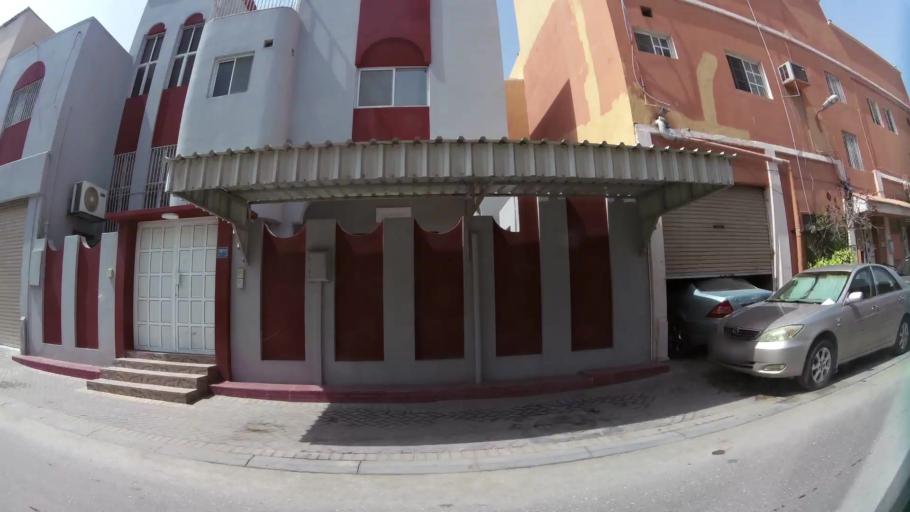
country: BH
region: Manama
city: Jidd Hafs
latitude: 26.2270
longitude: 50.4805
